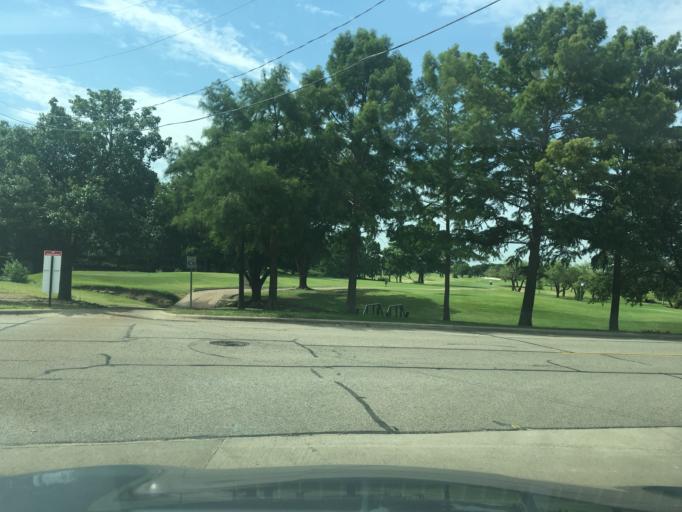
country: US
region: Texas
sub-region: Dallas County
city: Carrollton
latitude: 32.9425
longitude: -96.8633
